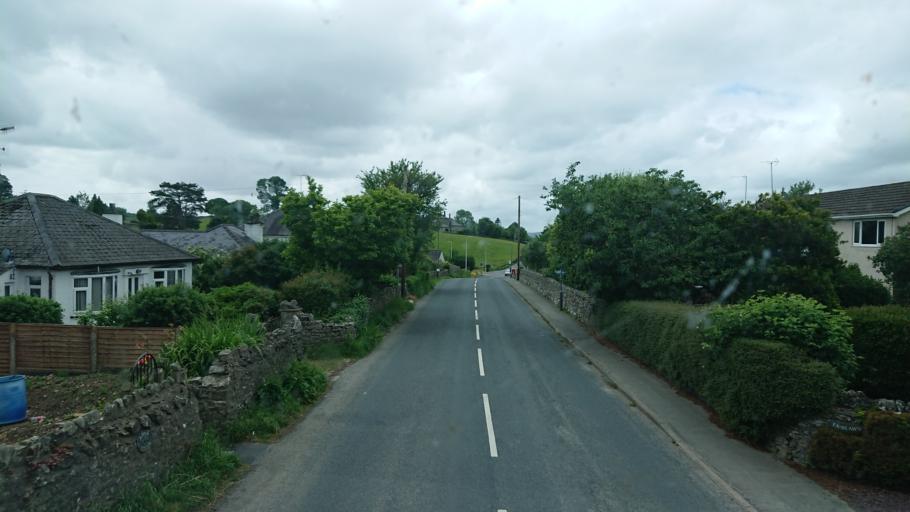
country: GB
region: England
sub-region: Cumbria
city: Milnthorpe
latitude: 54.2286
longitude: -2.7622
